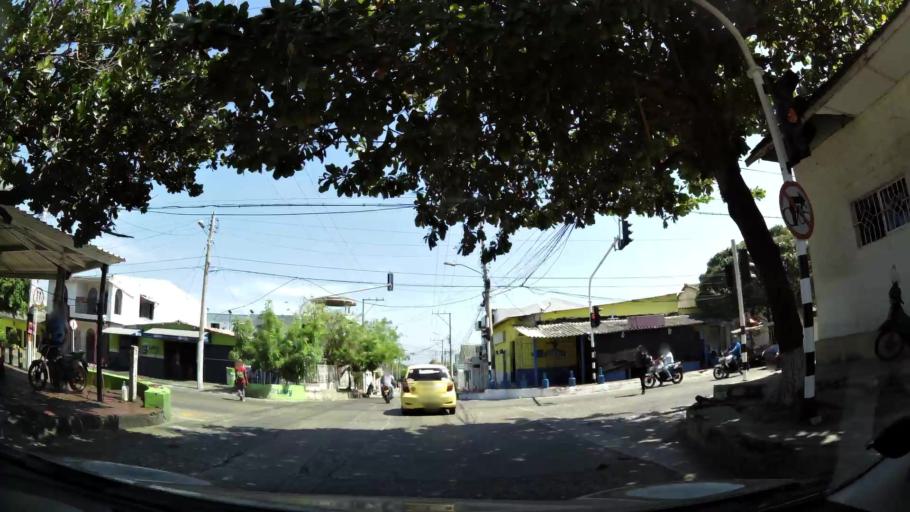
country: CO
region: Atlantico
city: Barranquilla
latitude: 10.9762
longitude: -74.7918
